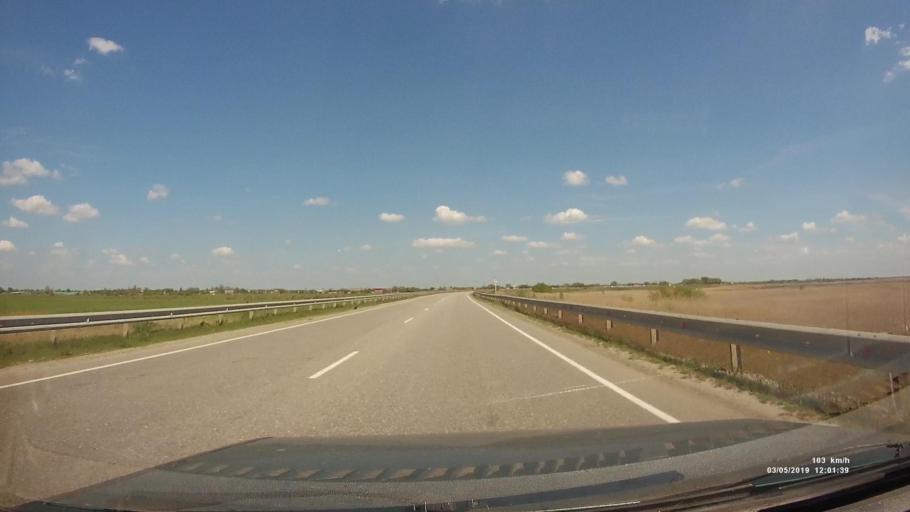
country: RU
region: Rostov
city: Bagayevskaya
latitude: 47.2655
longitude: 40.3529
